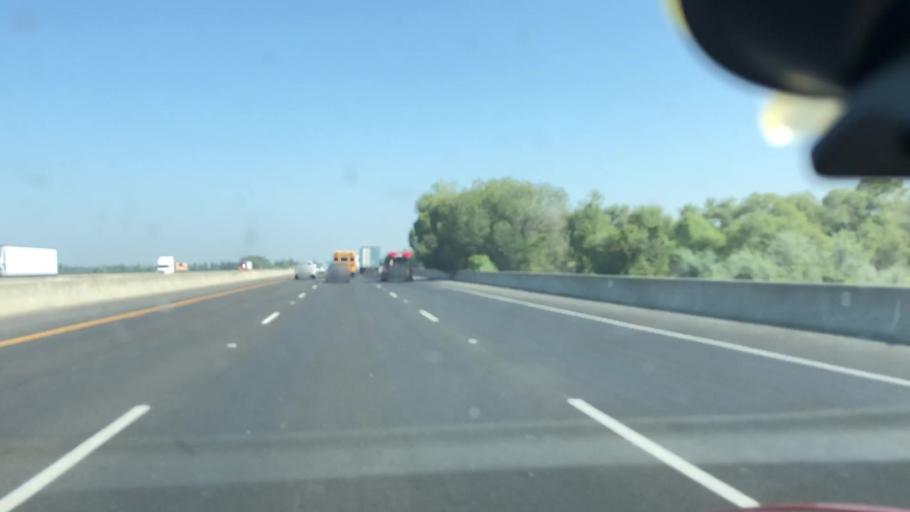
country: US
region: California
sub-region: Sacramento County
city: Parkway
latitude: 38.4391
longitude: -121.4899
